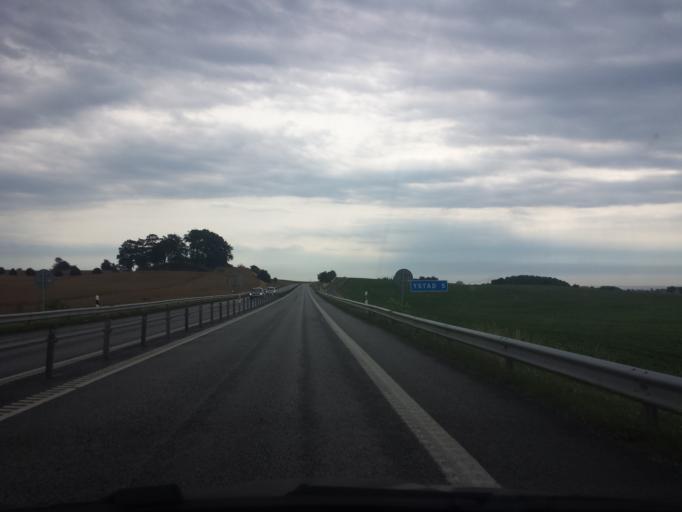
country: SE
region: Skane
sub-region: Ystads Kommun
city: Ystad
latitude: 55.4490
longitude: 13.7669
